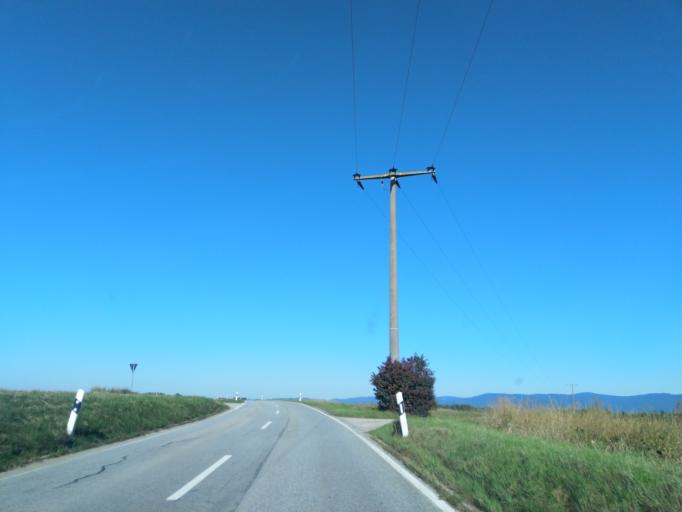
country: DE
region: Bavaria
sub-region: Lower Bavaria
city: Stephansposching
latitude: 48.8143
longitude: 12.8434
